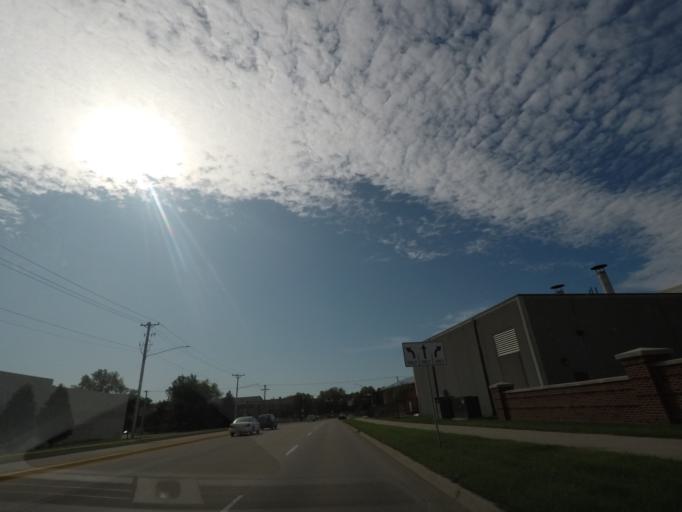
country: US
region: Iowa
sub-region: Story County
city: Ames
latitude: 42.0204
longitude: -93.6205
